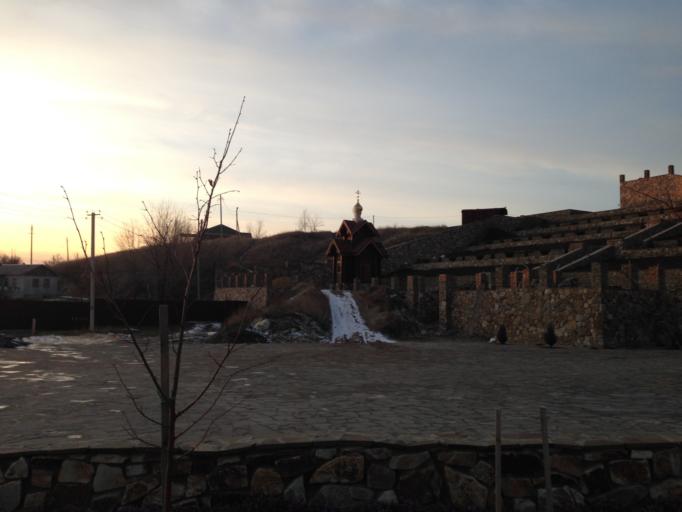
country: RU
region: Rostov
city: Staraya Stanitsa
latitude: 48.3496
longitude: 40.2916
